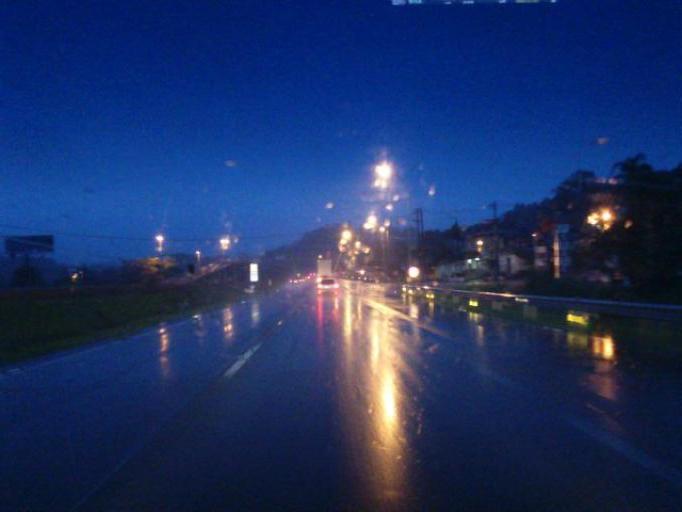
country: BR
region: Sao Paulo
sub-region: Juquitiba
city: Juquitiba
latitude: -23.9326
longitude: -47.0091
